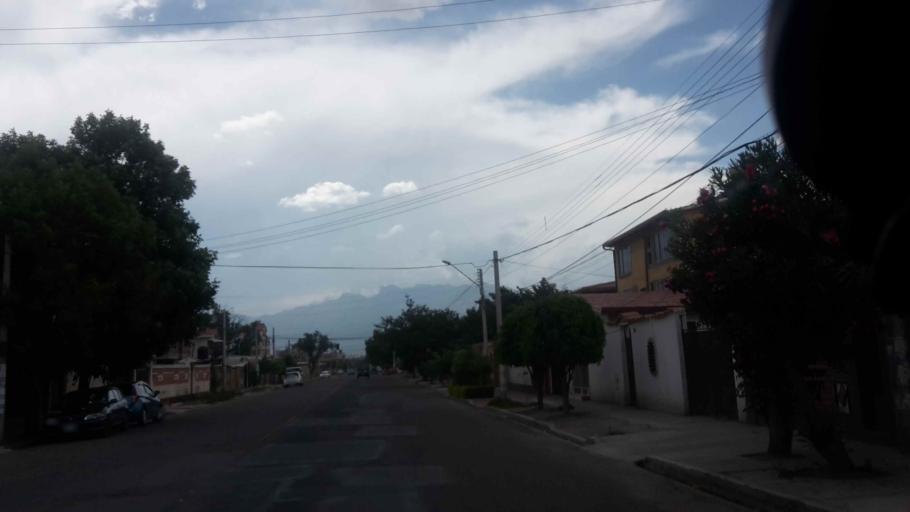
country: BO
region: Cochabamba
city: Cochabamba
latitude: -17.4054
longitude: -66.1736
